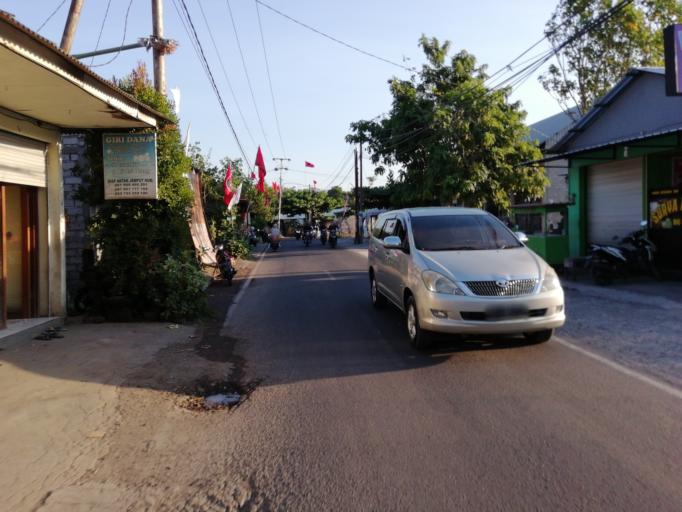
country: ID
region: Bali
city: Bualu
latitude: -8.7921
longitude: 115.1958
